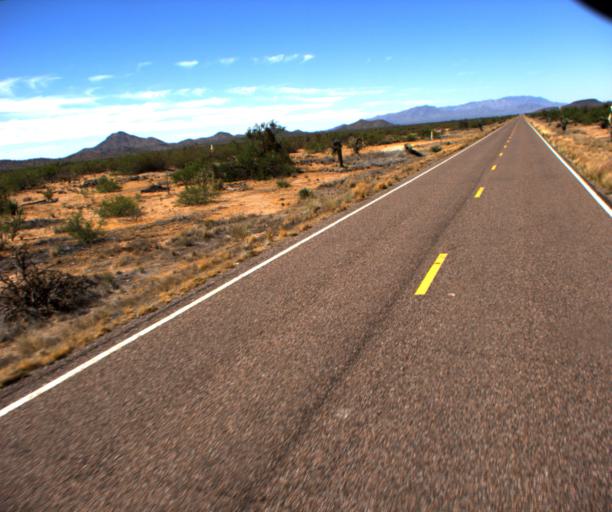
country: US
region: Arizona
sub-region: Yavapai County
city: Congress
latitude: 34.0532
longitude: -113.0550
